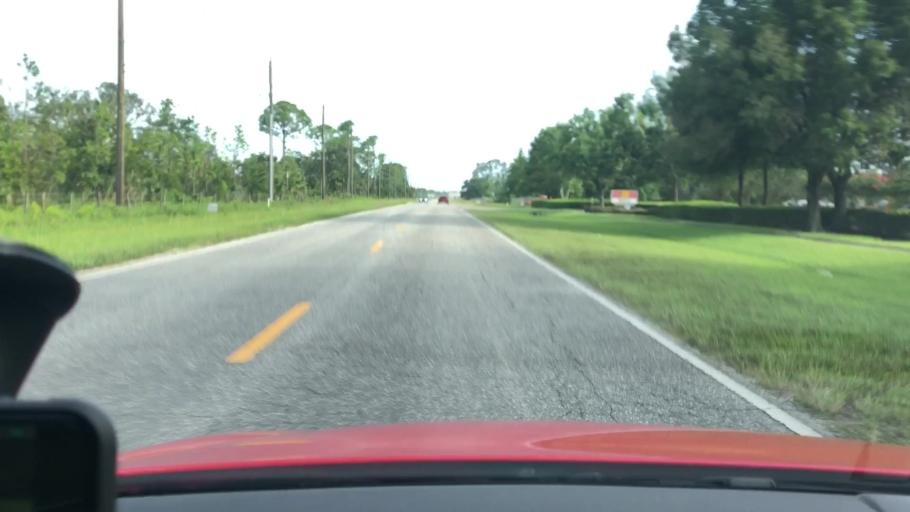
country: US
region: Florida
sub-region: Volusia County
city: Daytona Beach
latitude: 29.1796
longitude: -81.0915
